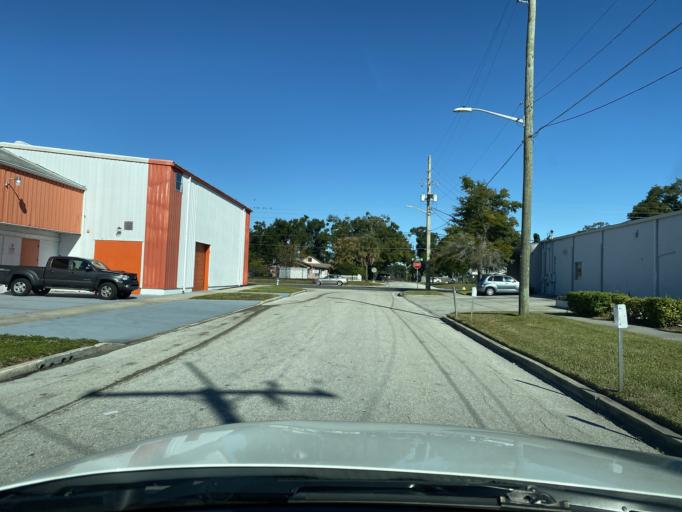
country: US
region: Florida
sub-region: Orange County
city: Orlando
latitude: 28.5433
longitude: -81.4004
